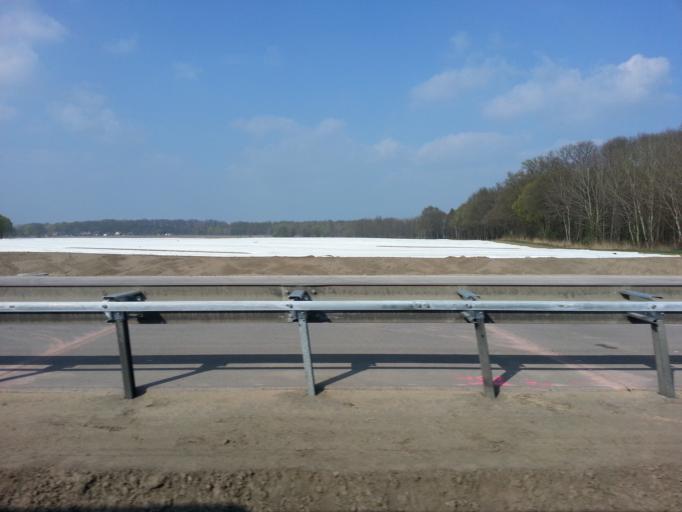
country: DE
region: Brandenburg
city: Kremmen
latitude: 52.7149
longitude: 12.9981
